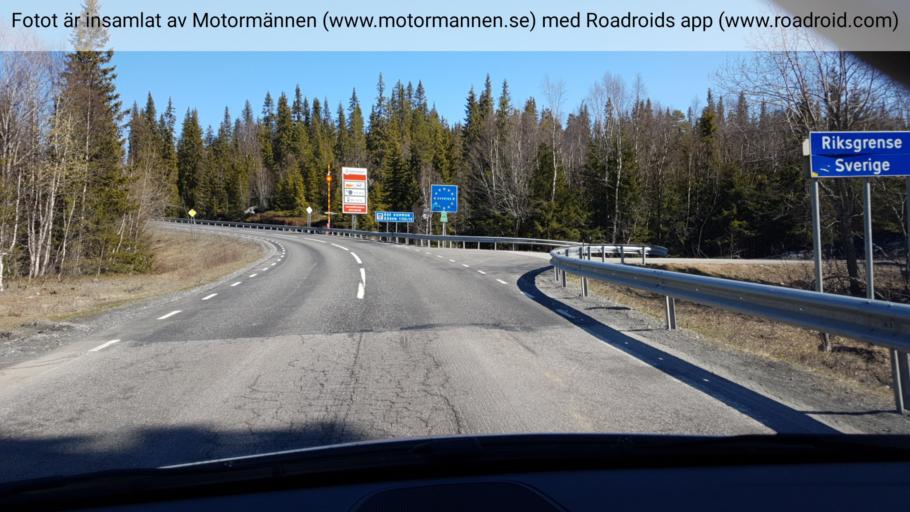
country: NO
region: Nord-Trondelag
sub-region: Meraker
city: Meraker
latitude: 63.6491
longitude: 12.2586
